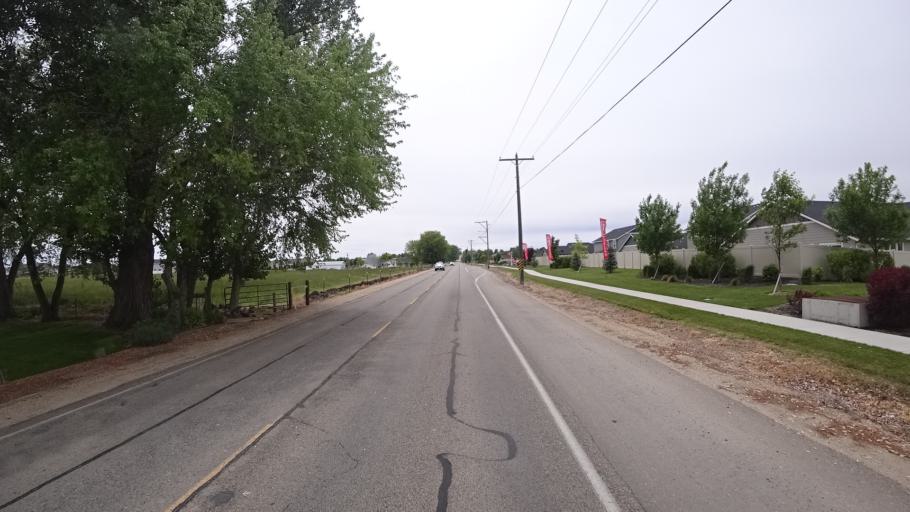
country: US
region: Idaho
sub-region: Ada County
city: Meridian
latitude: 43.5683
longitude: -116.3746
